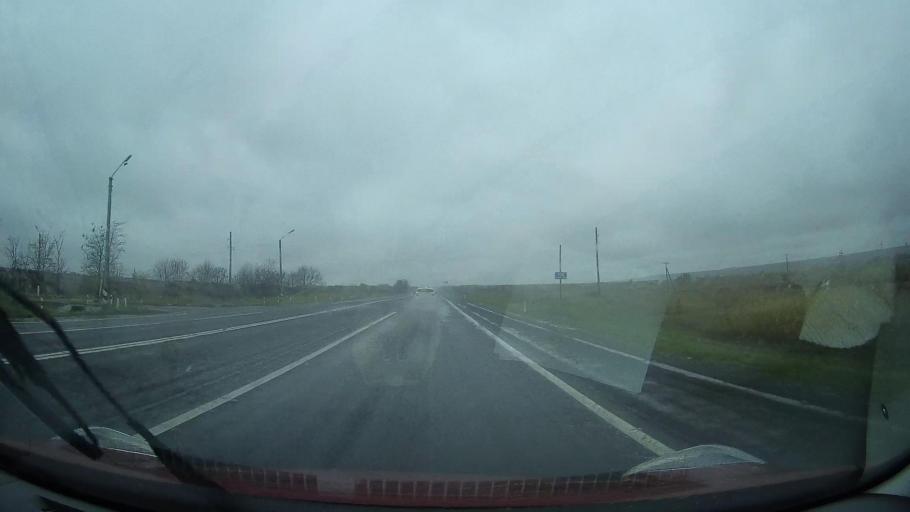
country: RU
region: Stavropol'skiy
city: Nevinnomyssk
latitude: 44.6229
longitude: 42.0743
